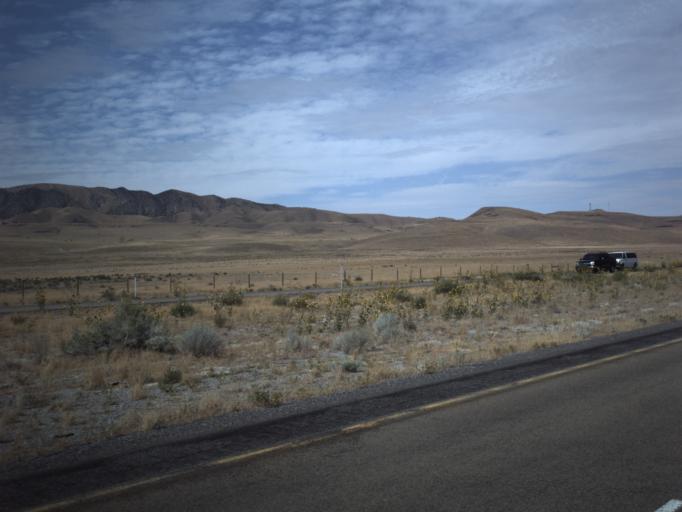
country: US
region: Utah
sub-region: Tooele County
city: Grantsville
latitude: 40.7881
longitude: -112.8273
